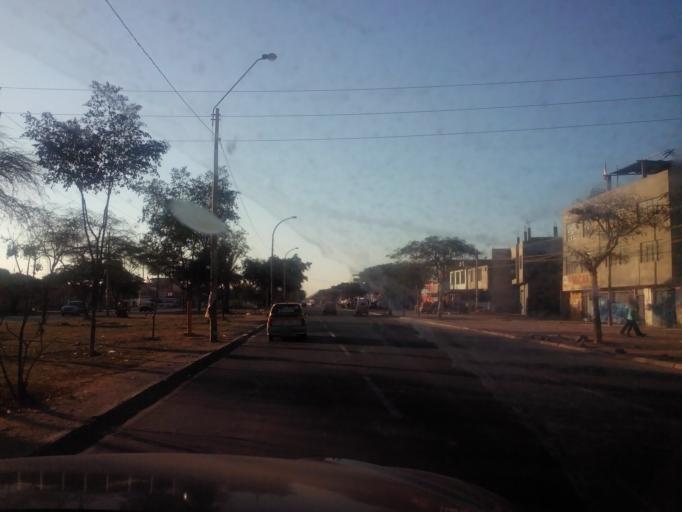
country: PE
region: Ica
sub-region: Provincia de Ica
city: Ica
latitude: -14.0641
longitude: -75.7406
